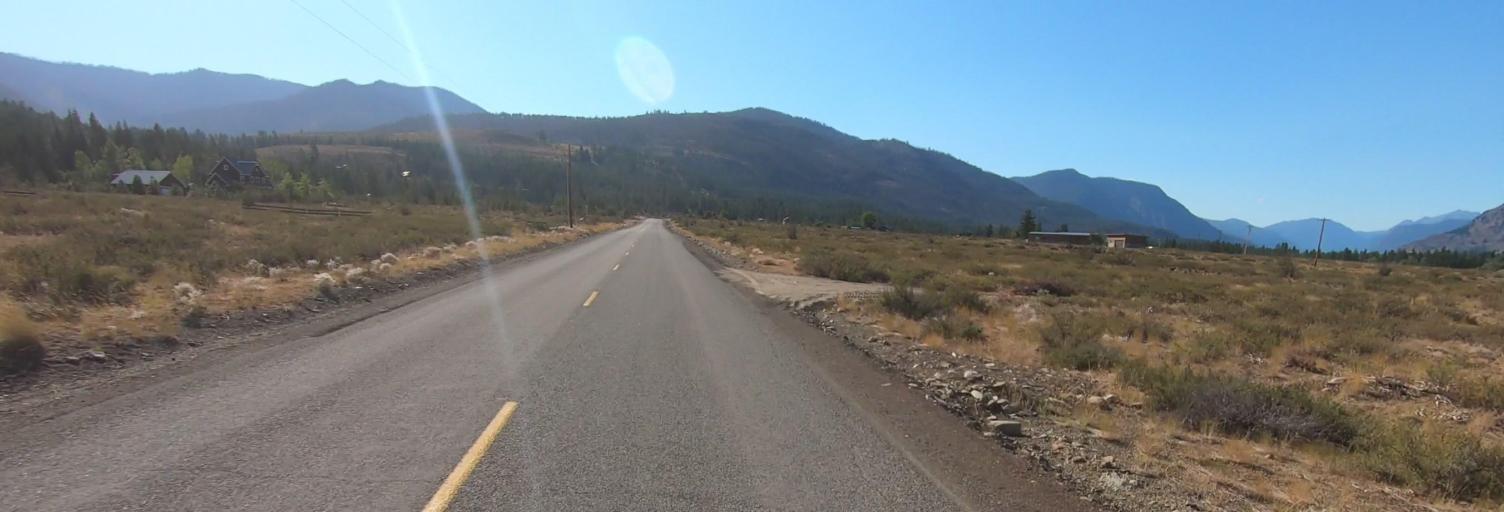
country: US
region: Washington
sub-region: Chelan County
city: Granite Falls
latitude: 48.4906
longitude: -120.2430
